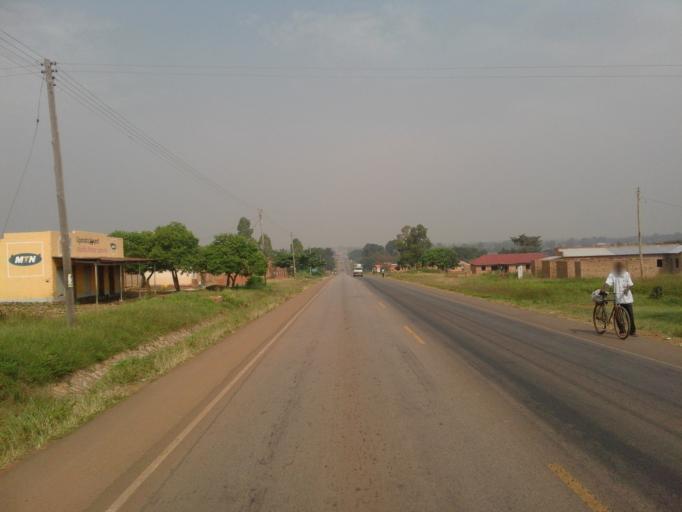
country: UG
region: Eastern Region
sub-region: Bugiri District
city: Bugiri
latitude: 0.5589
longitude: 33.7612
